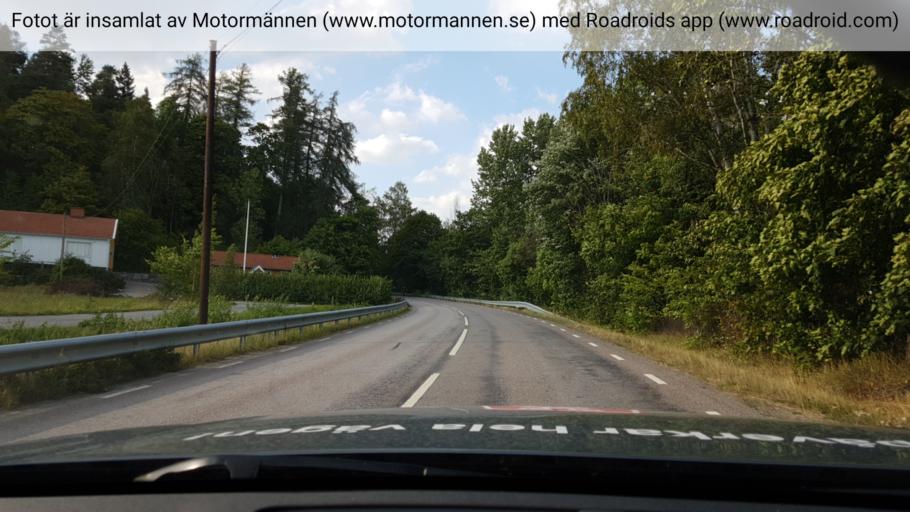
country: SE
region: Soedermanland
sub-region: Gnesta Kommun
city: Gnesta
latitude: 59.0596
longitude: 17.3043
